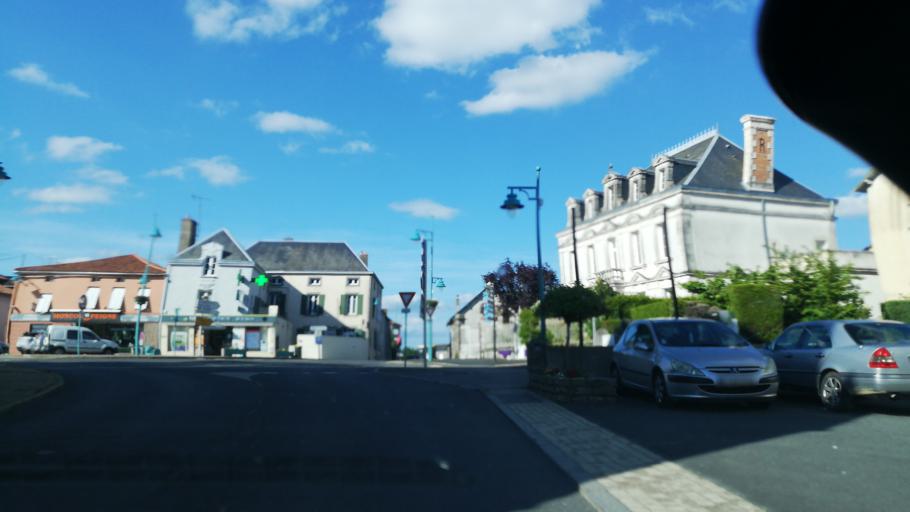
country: FR
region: Poitou-Charentes
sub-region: Departement des Deux-Sevres
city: Moncoutant
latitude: 46.7223
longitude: -0.5869
